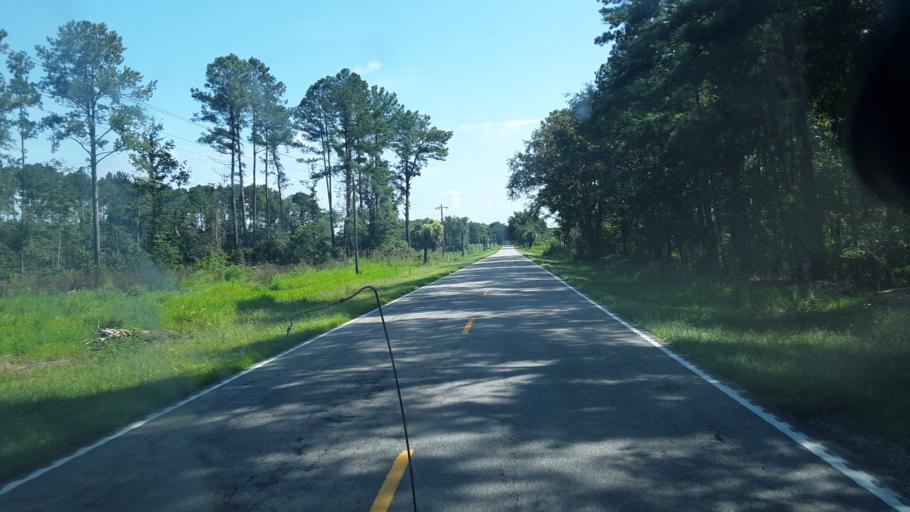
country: US
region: South Carolina
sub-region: Hampton County
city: Varnville
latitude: 32.8954
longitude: -81.0101
